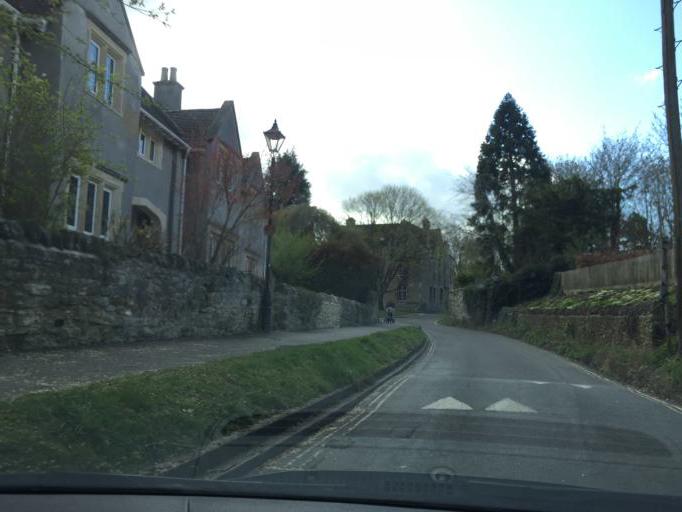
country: GB
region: England
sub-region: Oxfordshire
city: Cowley
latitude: 51.7652
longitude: -1.2141
